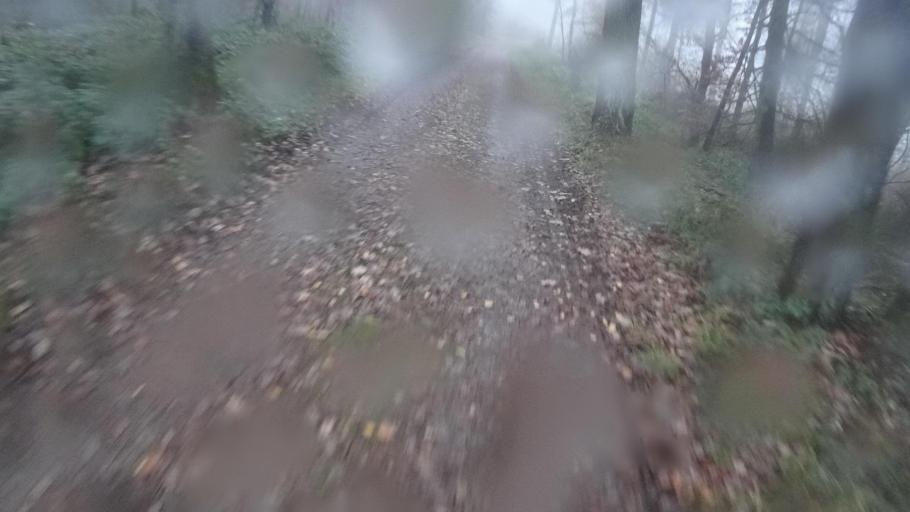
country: DE
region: Rheinland-Pfalz
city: Karbach
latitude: 50.1789
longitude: 7.6055
